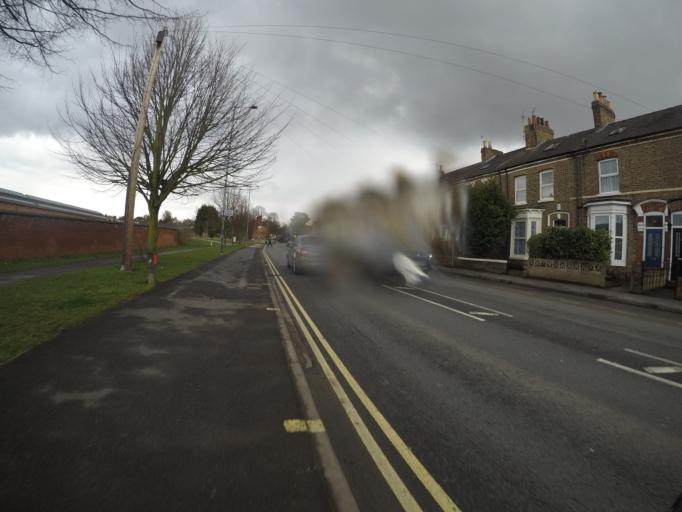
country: GB
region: England
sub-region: City of York
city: York
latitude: 53.9565
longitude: -1.1078
